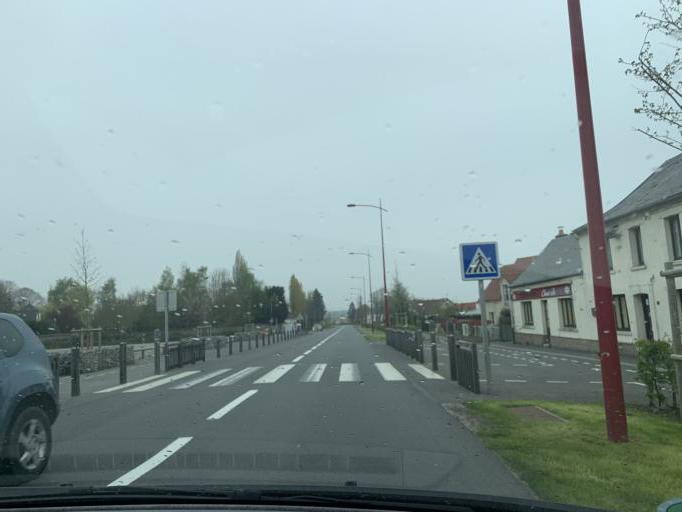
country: FR
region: Picardie
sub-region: Departement de la Somme
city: Nouvion
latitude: 50.1720
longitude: 1.8104
